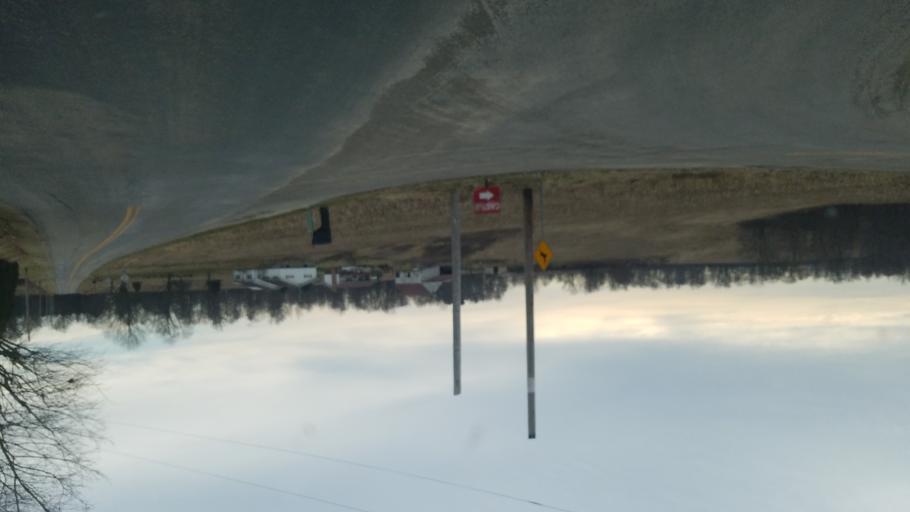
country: US
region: Ohio
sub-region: Ashland County
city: Loudonville
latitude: 40.5693
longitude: -82.2617
